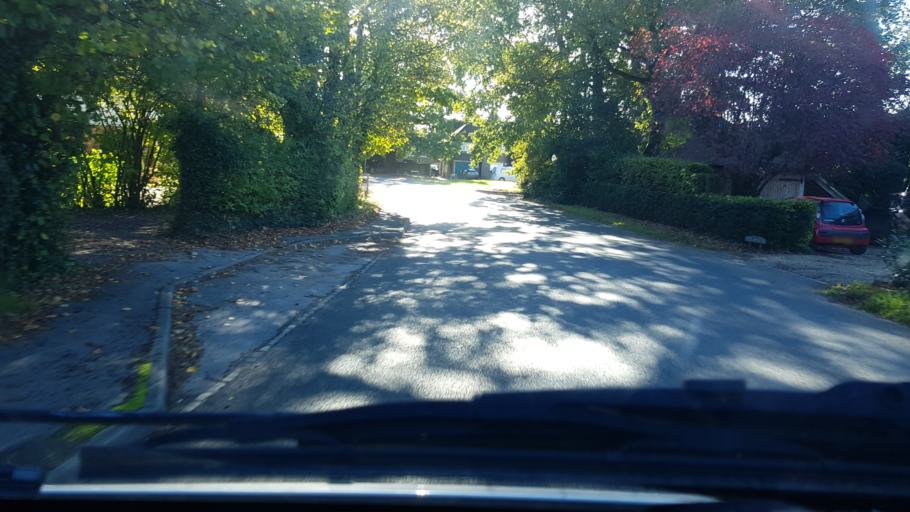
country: GB
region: England
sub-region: Surrey
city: Chilworth
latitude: 51.1876
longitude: -0.5288
